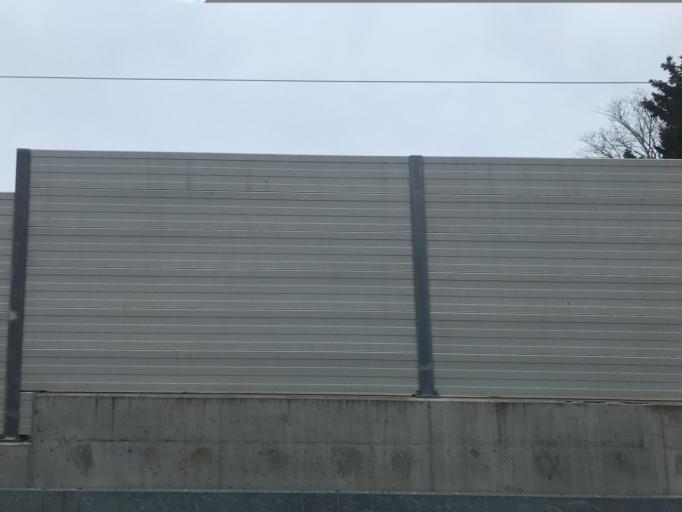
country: TR
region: Istanbul
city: Pendik
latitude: 40.8694
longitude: 29.2590
